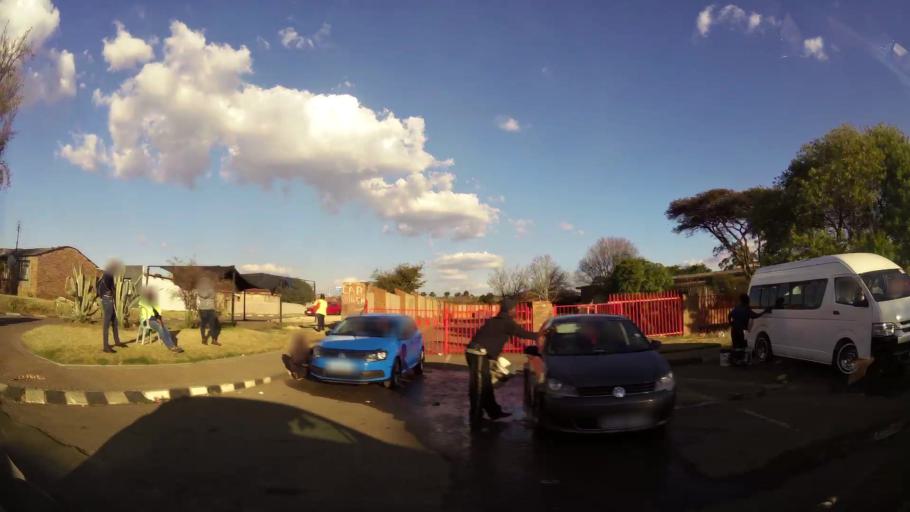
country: ZA
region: Mpumalanga
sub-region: Nkangala District Municipality
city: Witbank
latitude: -25.8813
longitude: 29.1900
